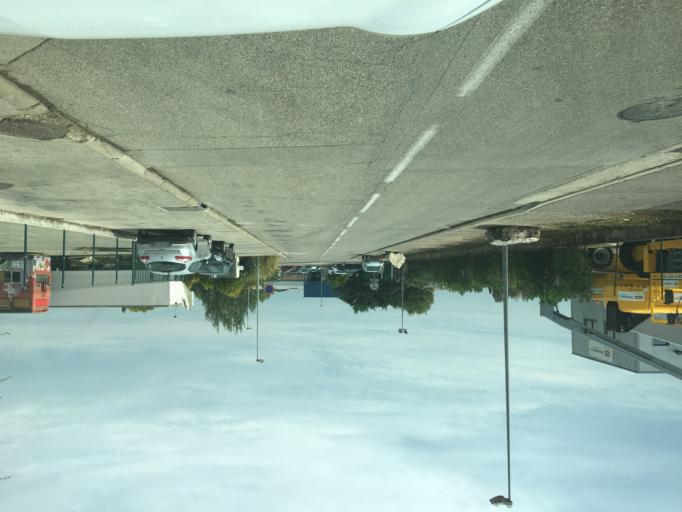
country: FR
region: Provence-Alpes-Cote d'Azur
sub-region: Departement des Bouches-du-Rhone
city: Bouc-Bel-Air
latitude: 43.4841
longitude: 5.3860
